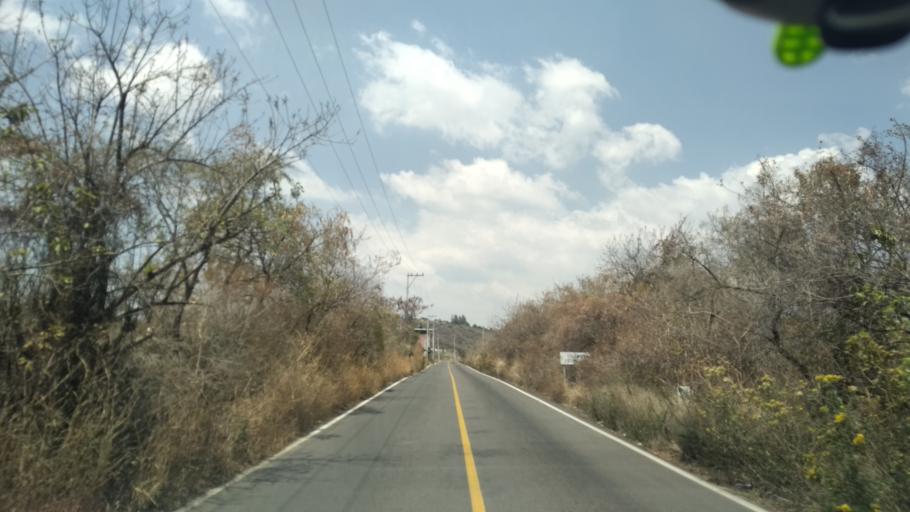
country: MX
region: Puebla
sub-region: Atzitzihuacan
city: Santiago Atzitzihuacan
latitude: 18.8330
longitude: -98.5915
